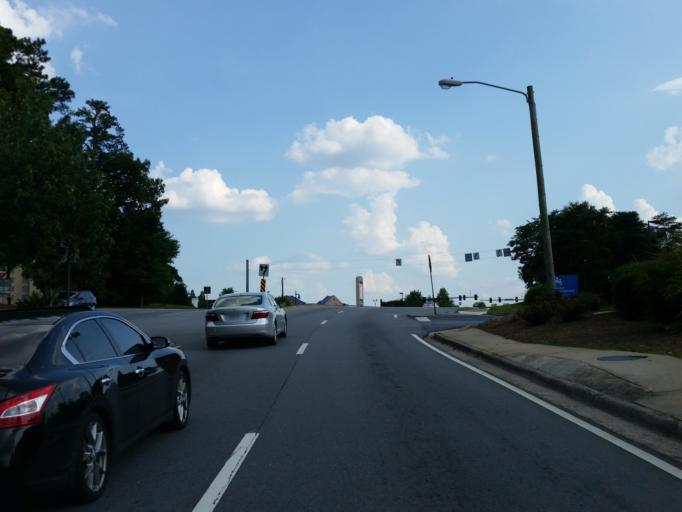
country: US
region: Georgia
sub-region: Cobb County
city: Vinings
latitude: 33.8671
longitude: -84.4768
